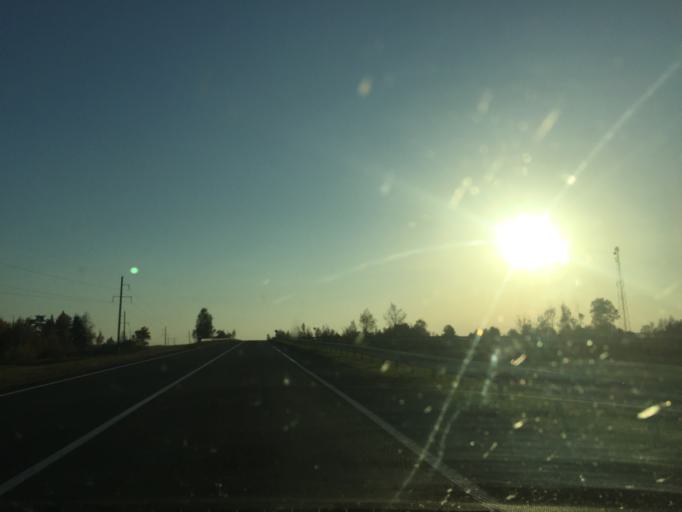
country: BY
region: Mogilev
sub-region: Mahilyowski Rayon
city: Veyno
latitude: 53.8149
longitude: 30.4604
